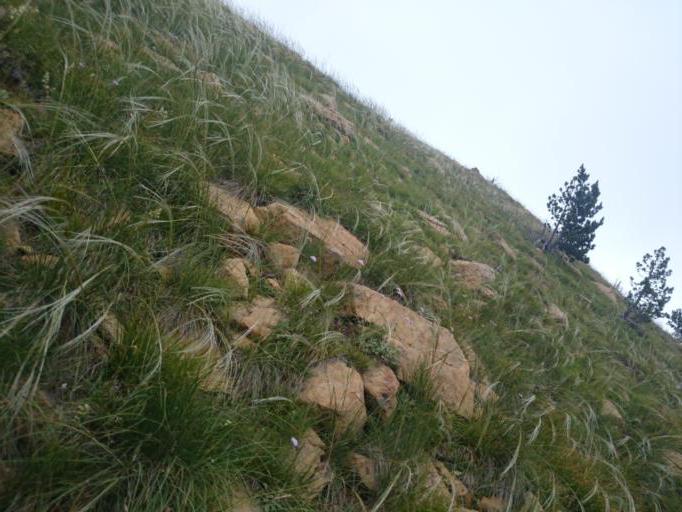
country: AL
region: Diber
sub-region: Rrethi i Dibres
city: Fushe-Lure
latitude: 41.7824
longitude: 20.1840
